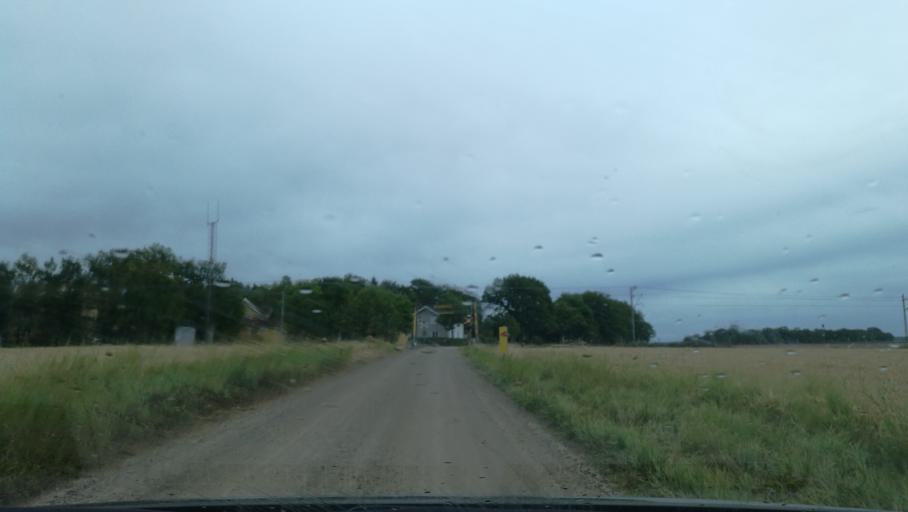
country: SE
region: Vaestmanland
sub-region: Vasteras
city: Tillberga
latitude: 59.7169
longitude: 16.6414
